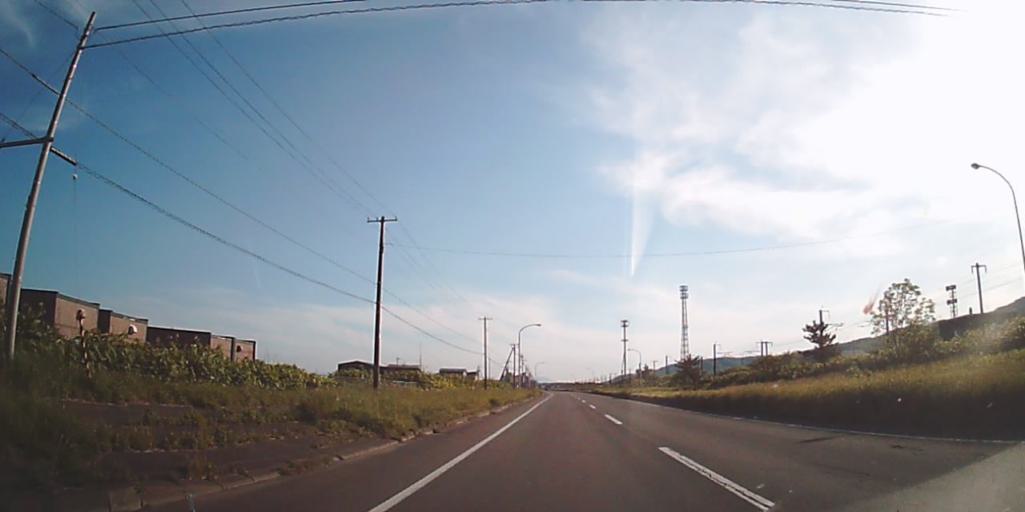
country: JP
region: Hokkaido
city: Muroran
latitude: 42.4018
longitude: 141.0981
